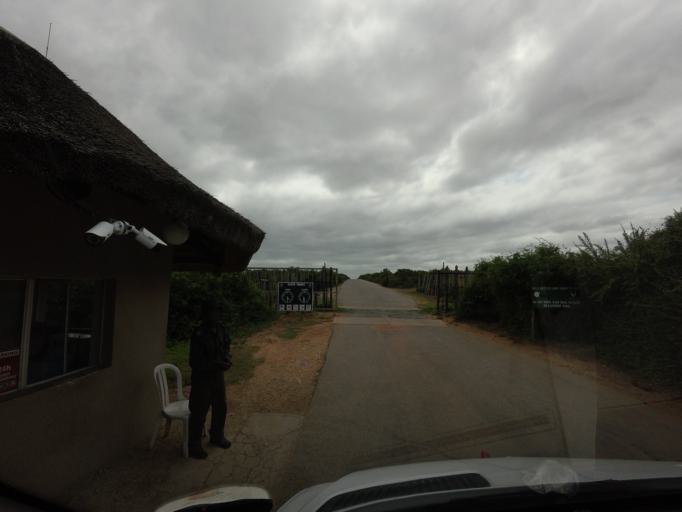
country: ZA
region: Eastern Cape
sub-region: Cacadu District Municipality
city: Kirkwood
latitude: -33.4416
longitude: 25.7504
